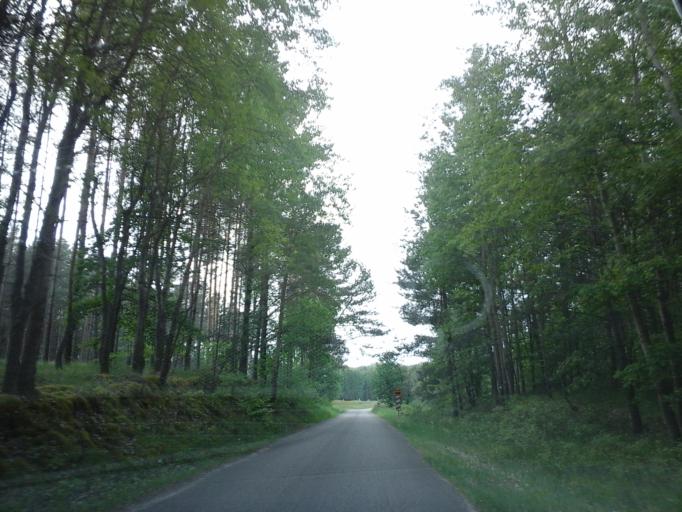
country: PL
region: West Pomeranian Voivodeship
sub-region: Powiat walecki
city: Tuczno
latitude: 53.2269
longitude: 16.0630
